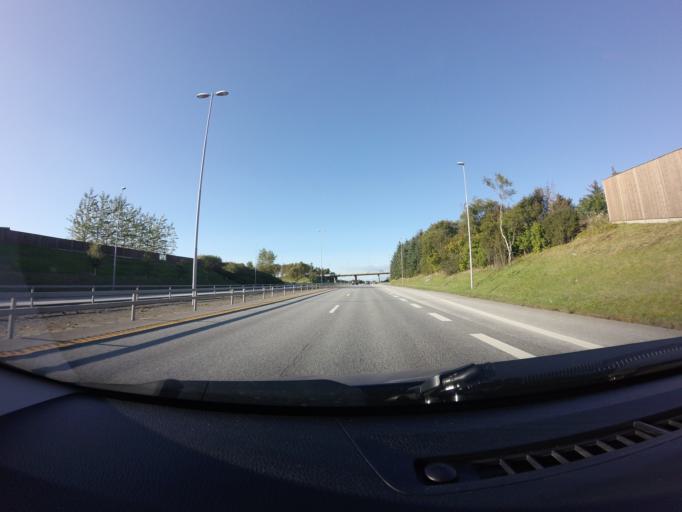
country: NO
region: Rogaland
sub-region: Sandnes
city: Sandnes
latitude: 58.8554
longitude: 5.7133
